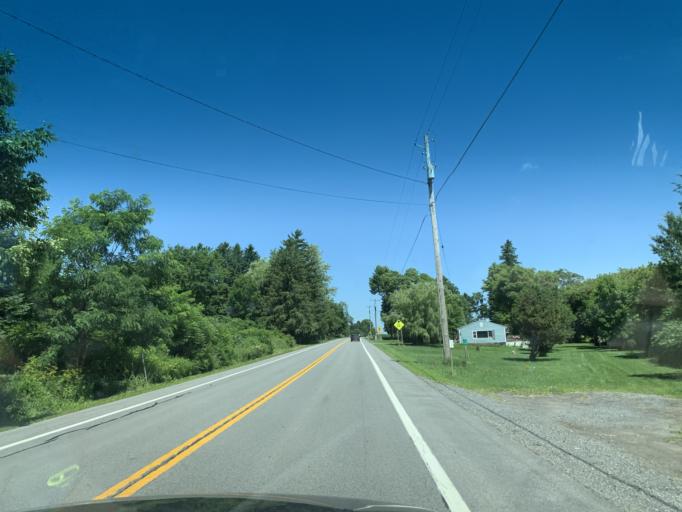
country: US
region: New York
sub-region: Oneida County
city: Chadwicks
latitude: 42.9258
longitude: -75.2475
